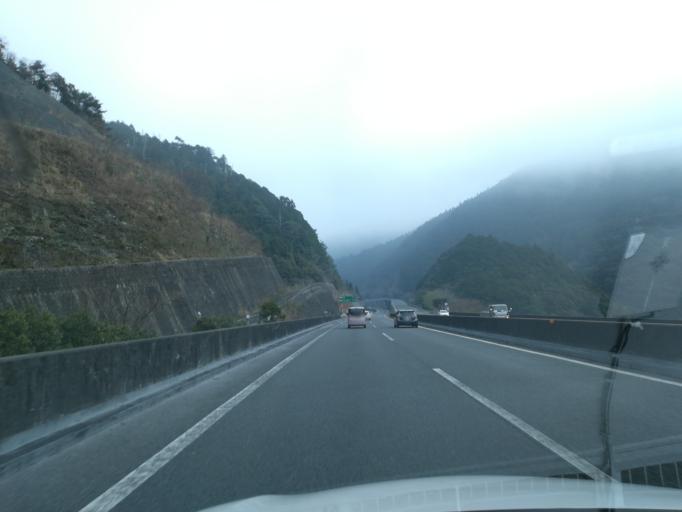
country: JP
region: Ehime
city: Kawanoecho
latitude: 33.7857
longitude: 133.6630
